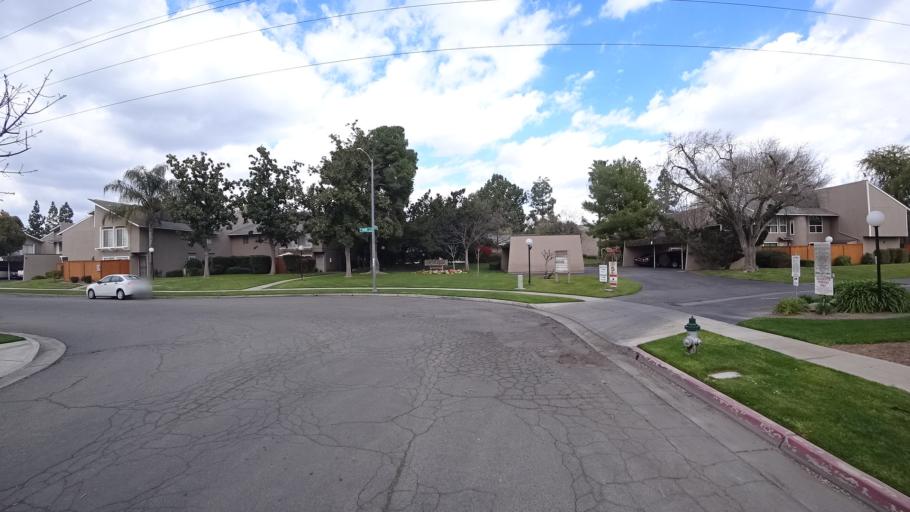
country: US
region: California
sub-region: Fresno County
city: Clovis
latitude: 36.8348
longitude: -119.7690
